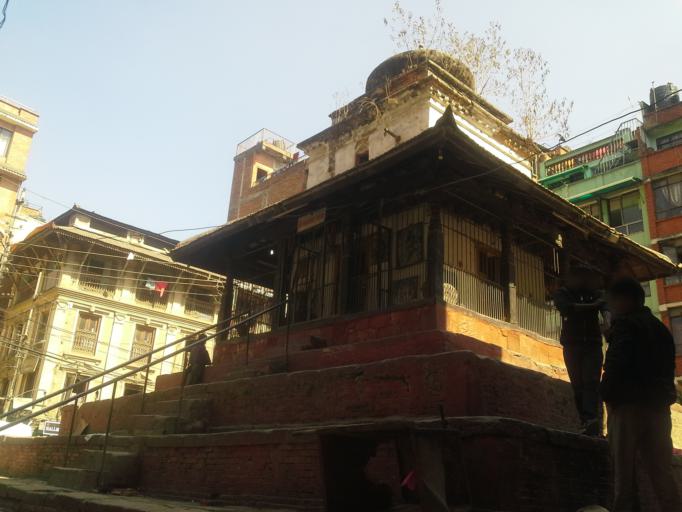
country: NP
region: Central Region
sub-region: Bagmati Zone
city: Kathmandu
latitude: 27.7068
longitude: 85.3098
